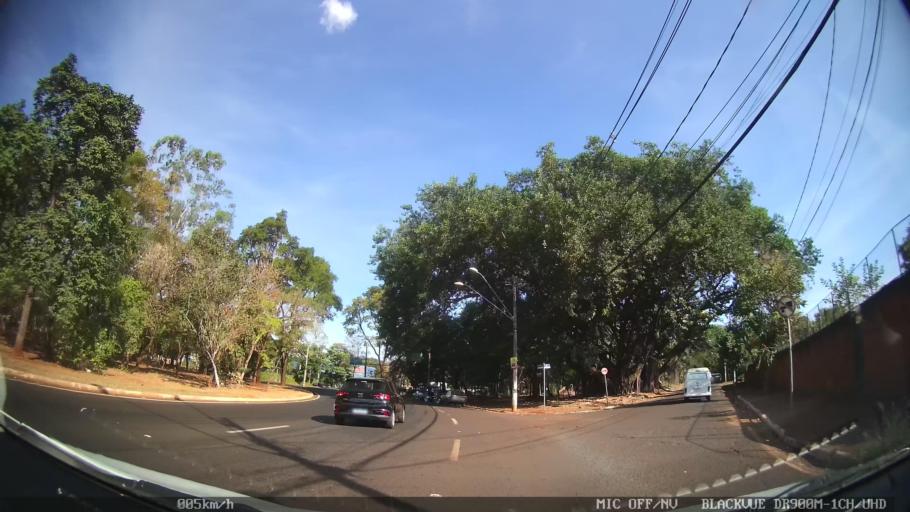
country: BR
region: Sao Paulo
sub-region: Ribeirao Preto
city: Ribeirao Preto
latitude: -21.1931
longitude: -47.7618
